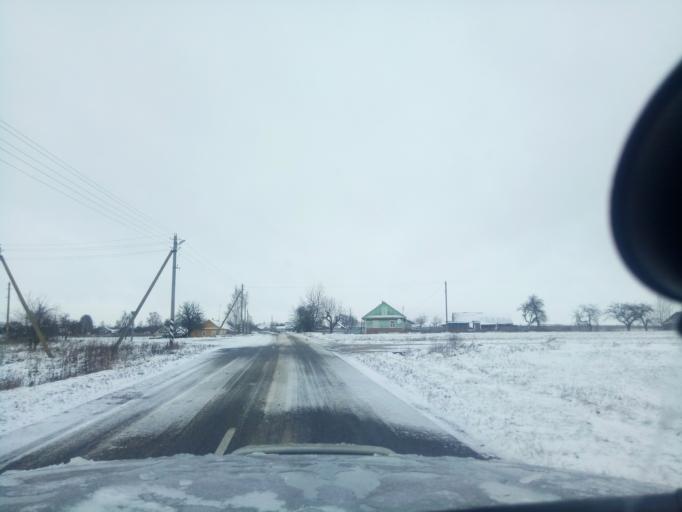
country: BY
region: Minsk
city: Klyetsk
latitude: 53.0168
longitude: 26.7103
